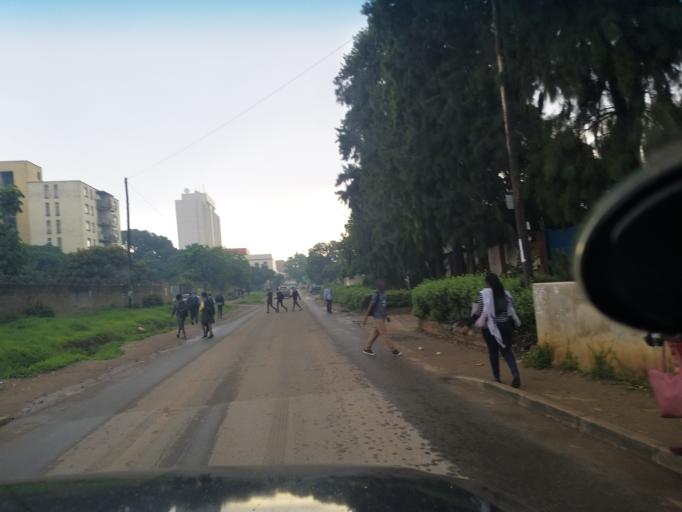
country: ZM
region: Lusaka
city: Lusaka
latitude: -15.4212
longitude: 28.2937
